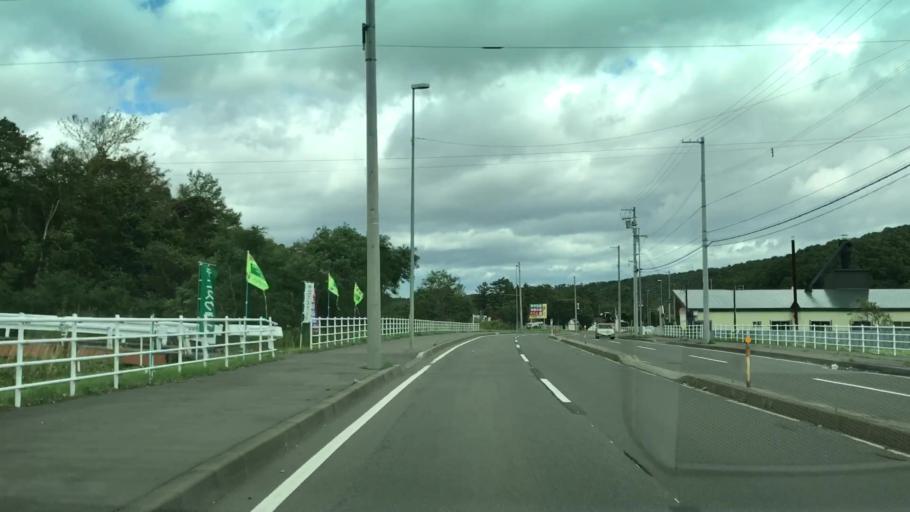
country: JP
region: Hokkaido
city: Kitahiroshima
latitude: 42.9638
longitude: 141.4548
